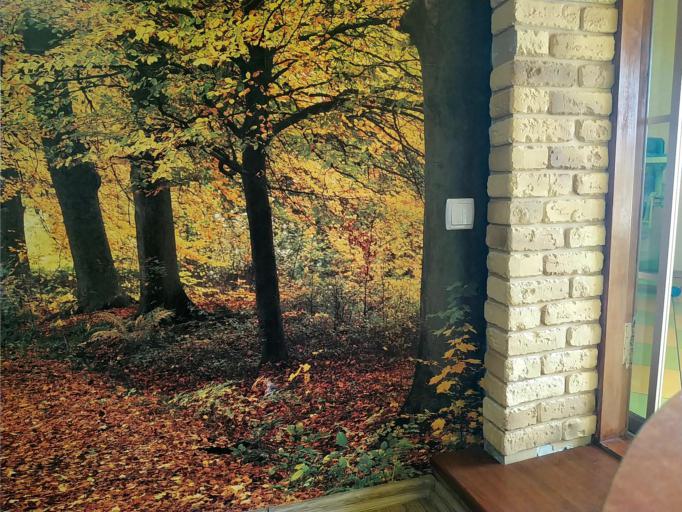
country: RU
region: Smolensk
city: Safonovo
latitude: 55.1132
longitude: 33.1780
